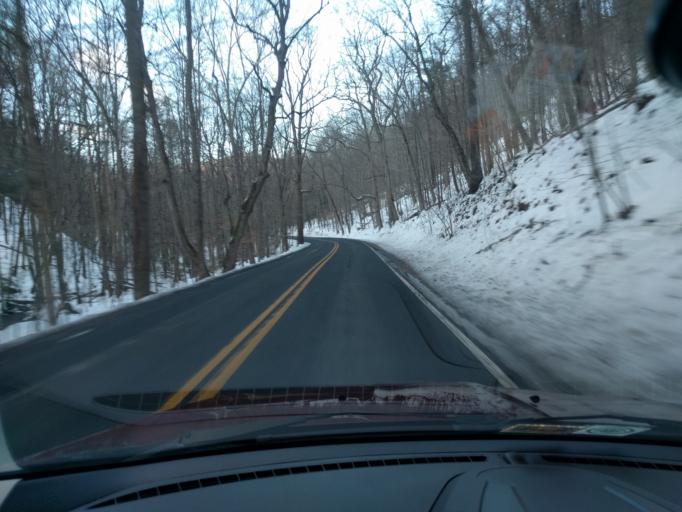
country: US
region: Virginia
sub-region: Bath County
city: Warm Springs
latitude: 38.0725
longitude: -79.8787
